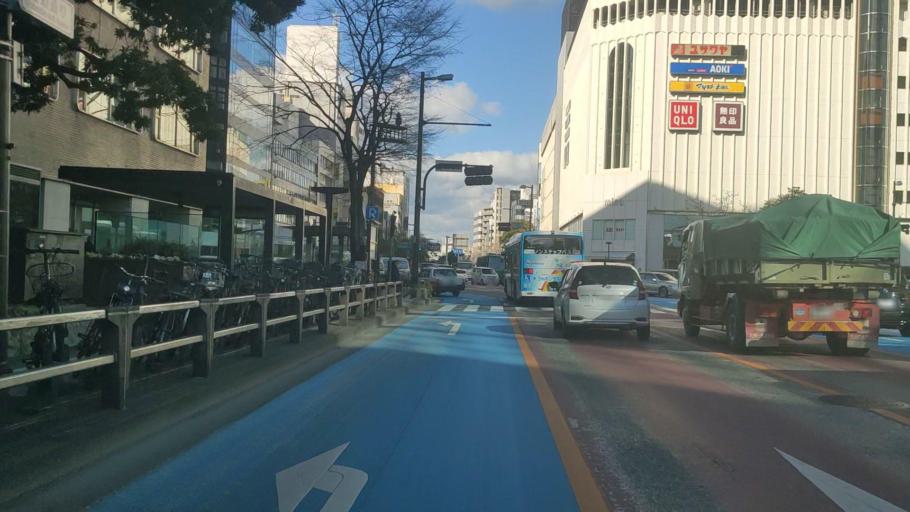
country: JP
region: Fukuoka
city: Fukuoka-shi
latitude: 33.5918
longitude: 130.3987
